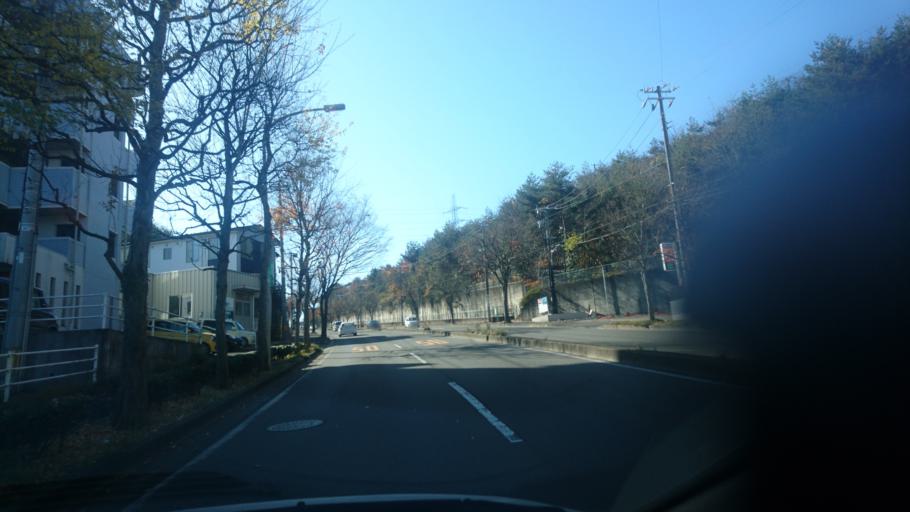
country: JP
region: Miyagi
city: Sendai-shi
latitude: 38.3050
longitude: 140.8317
